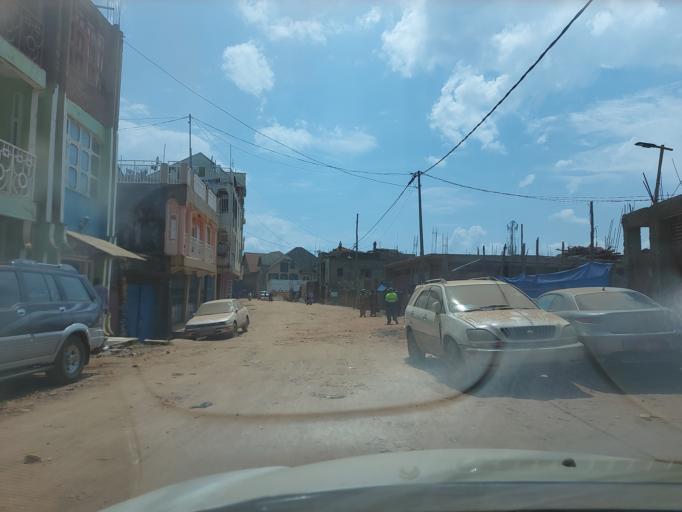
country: CD
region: South Kivu
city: Bukavu
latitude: -2.5022
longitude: 28.8628
